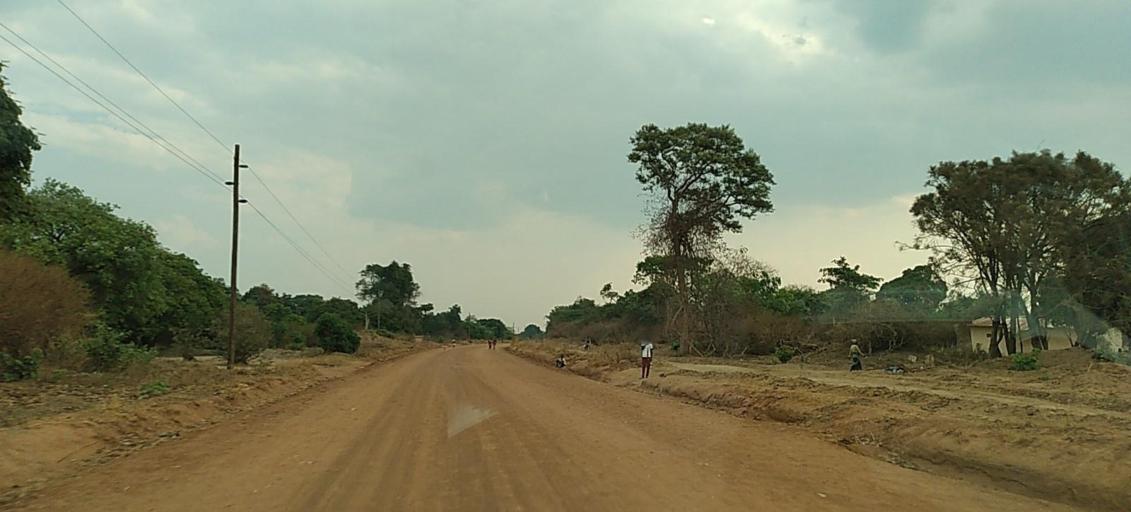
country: ZM
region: Copperbelt
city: Kalulushi
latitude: -12.8976
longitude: 27.9495
